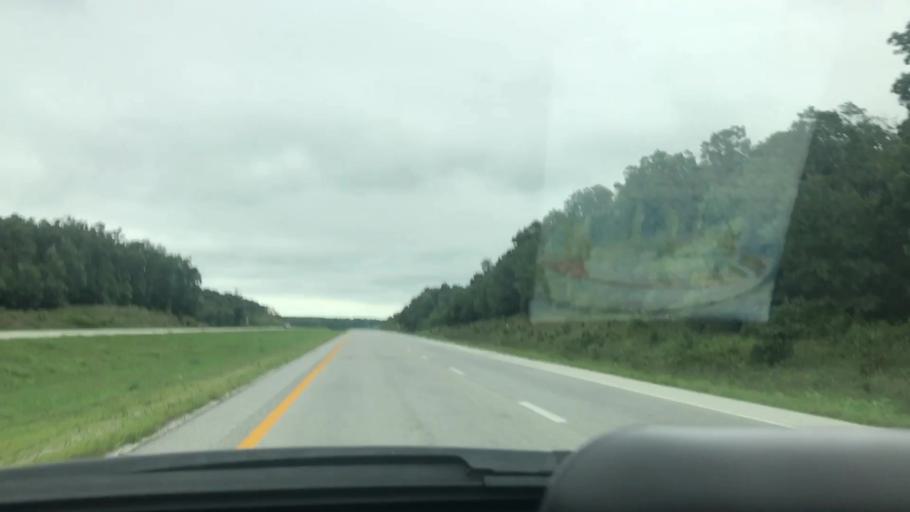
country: US
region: Missouri
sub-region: Greene County
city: Strafford
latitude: 37.2849
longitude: -93.1946
